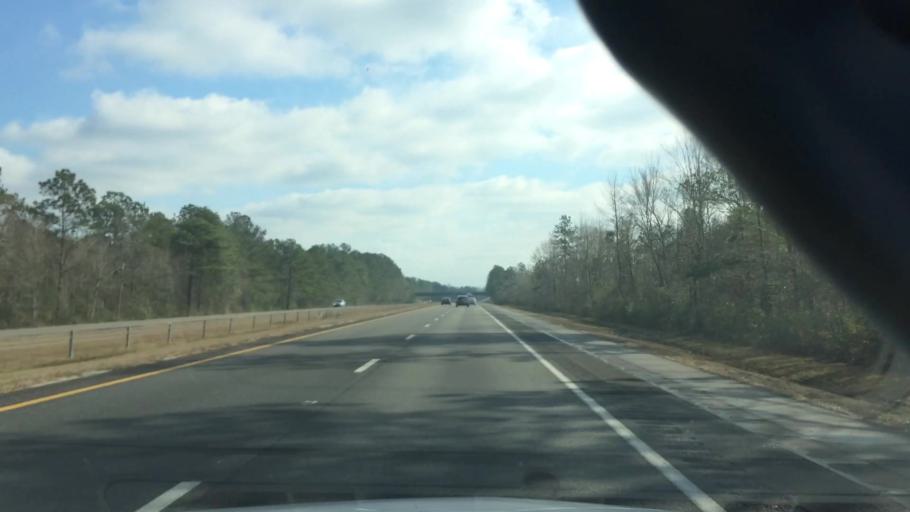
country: US
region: North Carolina
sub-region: Pender County
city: Burgaw
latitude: 34.6165
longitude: -77.9252
